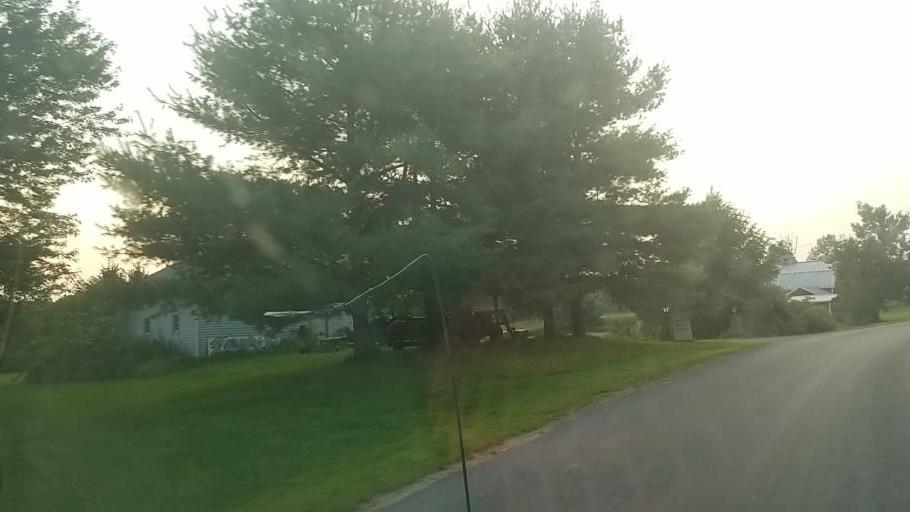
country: US
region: New York
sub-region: Montgomery County
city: Fonda
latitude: 42.9122
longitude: -74.3973
